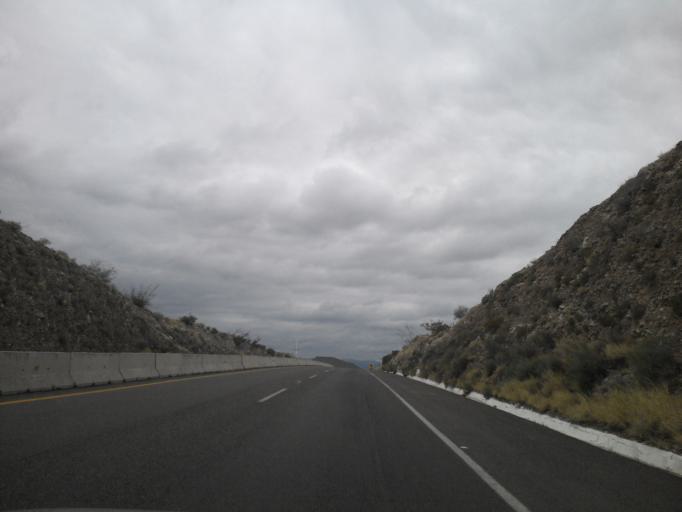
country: MX
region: Durango
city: Cuencame
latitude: 25.1470
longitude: -103.7519
